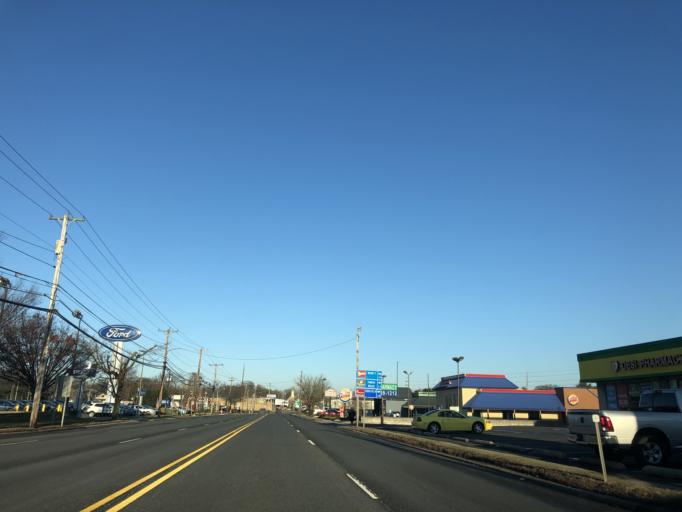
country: US
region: New Jersey
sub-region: Camden County
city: Lindenwold
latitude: 39.8319
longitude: -75.0034
